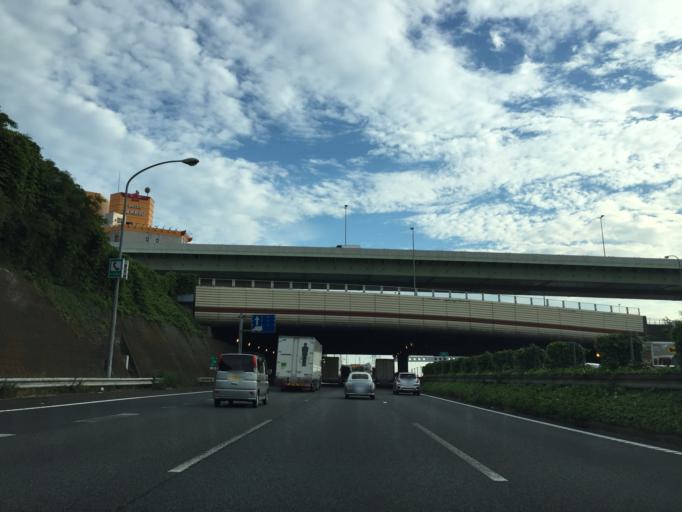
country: JP
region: Kanagawa
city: Minami-rinkan
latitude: 35.5064
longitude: 139.4829
